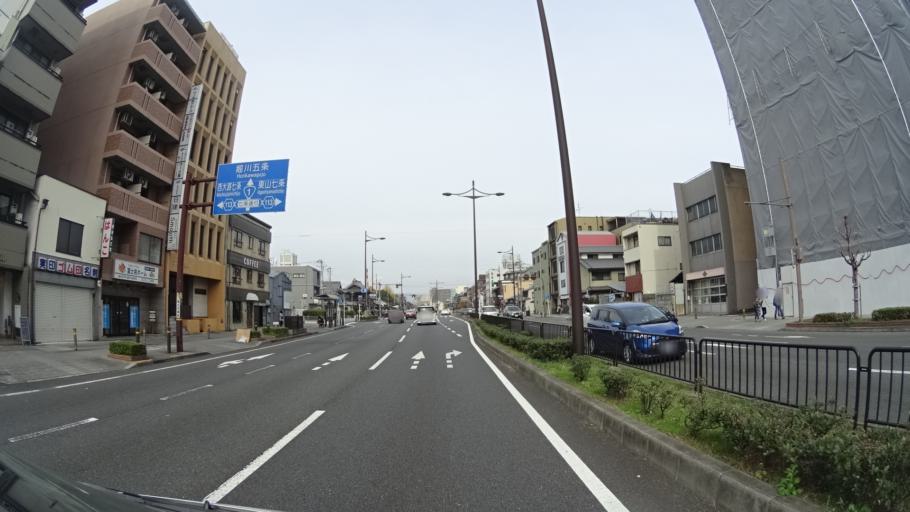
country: JP
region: Kyoto
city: Kyoto
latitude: 34.9880
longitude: 135.7530
